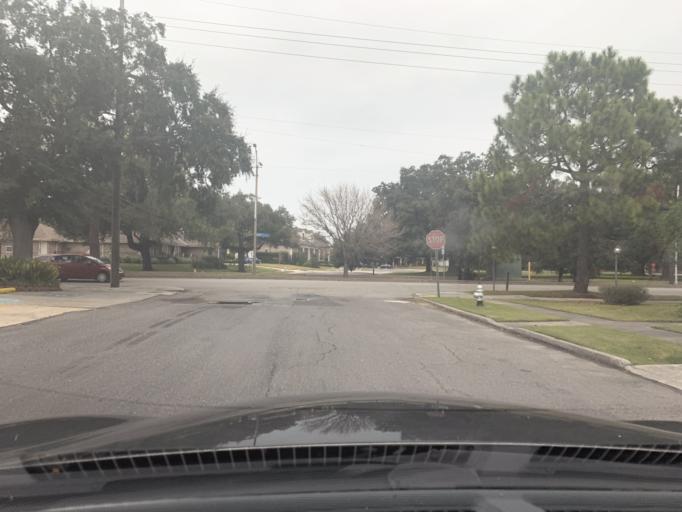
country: US
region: Louisiana
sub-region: Jefferson Parish
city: Metairie
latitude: 30.0193
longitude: -90.1076
